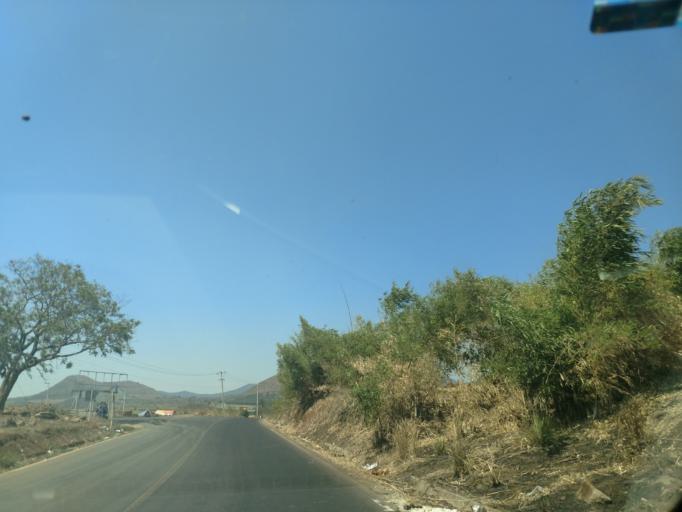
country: MX
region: Nayarit
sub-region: Tepic
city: La Corregidora
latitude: 21.4936
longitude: -104.7889
